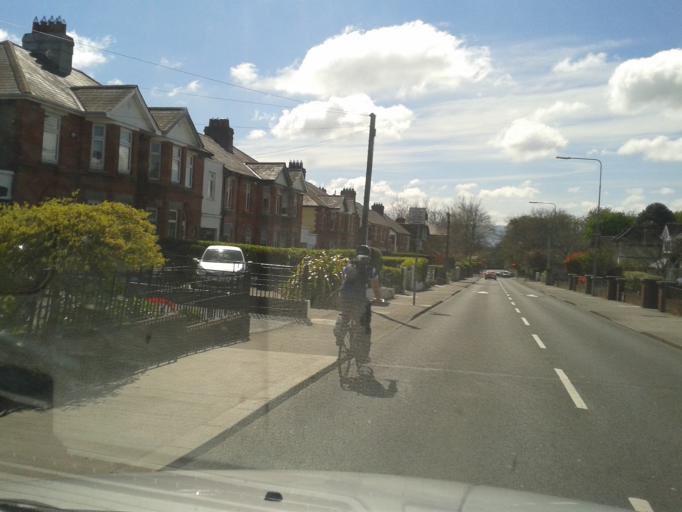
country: IE
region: Leinster
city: Marino
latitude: 53.3753
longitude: -6.2425
